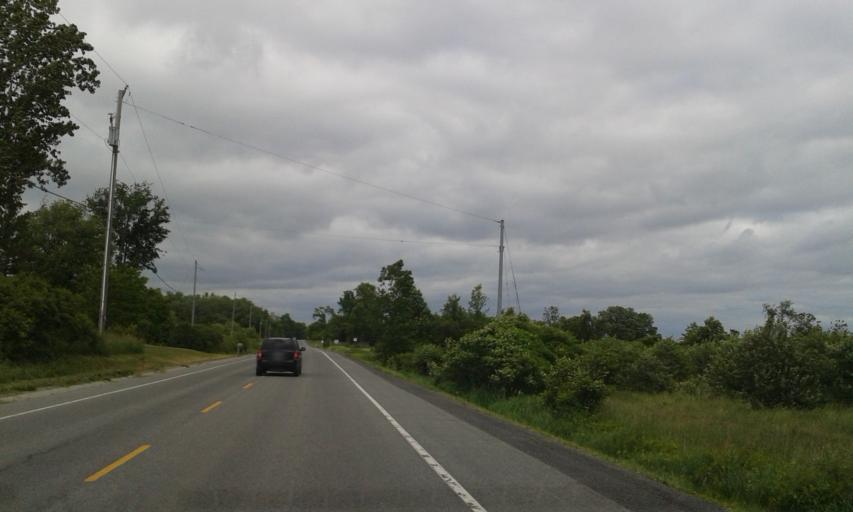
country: CA
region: Ontario
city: Deseronto
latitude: 44.0814
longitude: -76.9665
